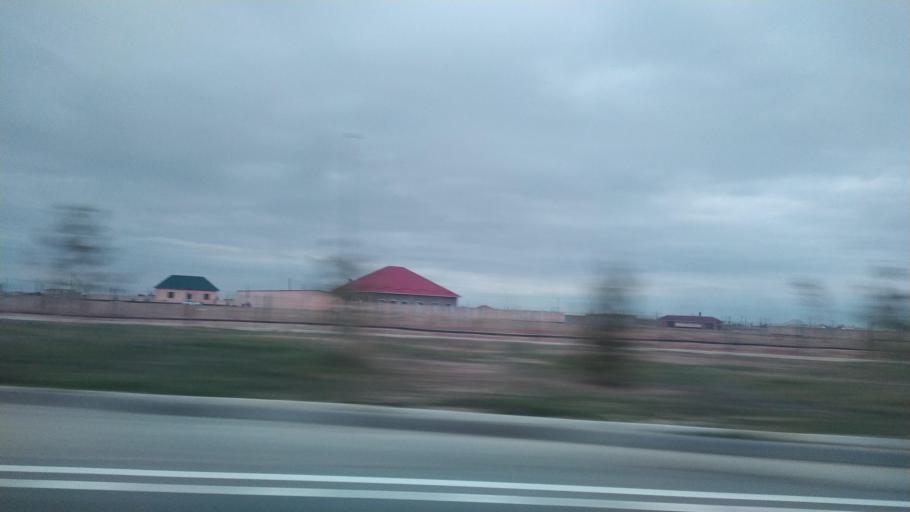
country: KZ
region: Ongtustik Qazaqstan
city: Turkestan
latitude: 43.2748
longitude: 68.4082
